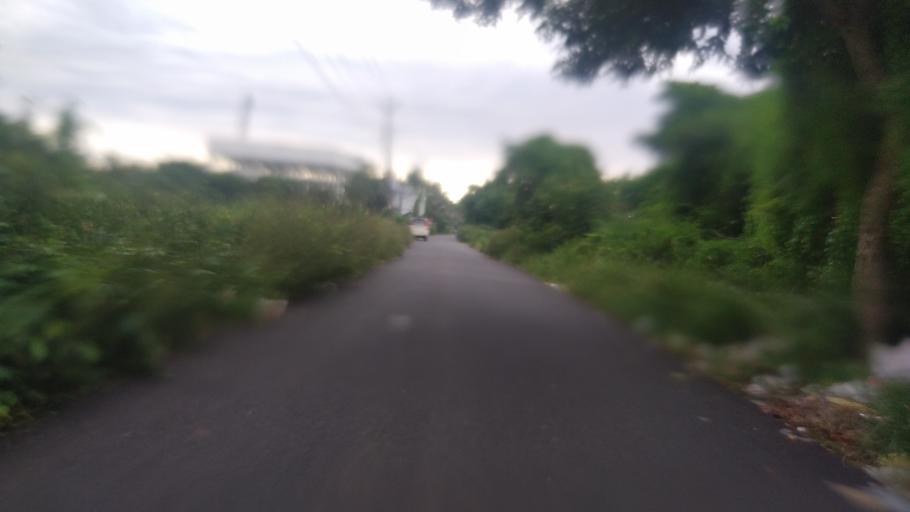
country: IN
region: Kerala
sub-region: Alappuzha
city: Arukutti
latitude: 9.8568
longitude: 76.2723
